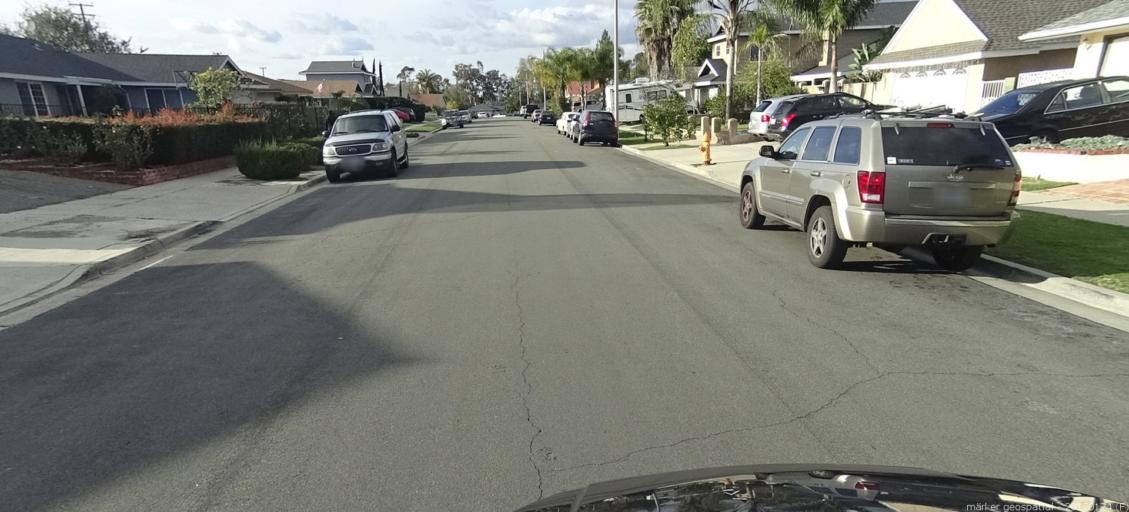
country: US
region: California
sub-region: Orange County
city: Lake Forest
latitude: 33.6297
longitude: -117.6981
